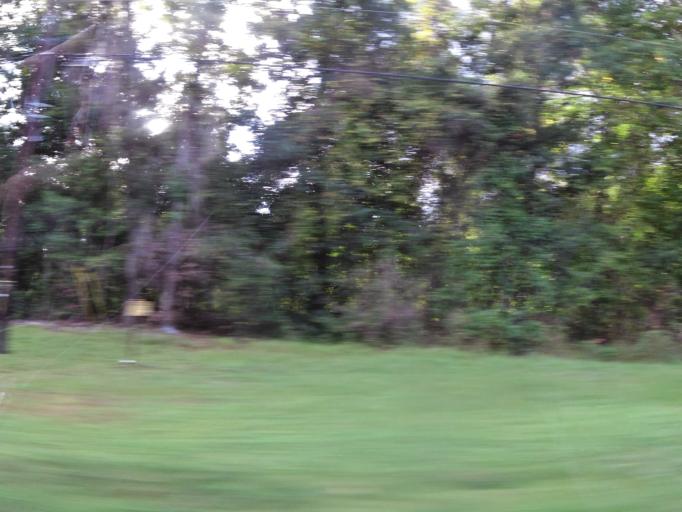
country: US
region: Georgia
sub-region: Liberty County
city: Midway
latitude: 31.8124
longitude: -81.4304
